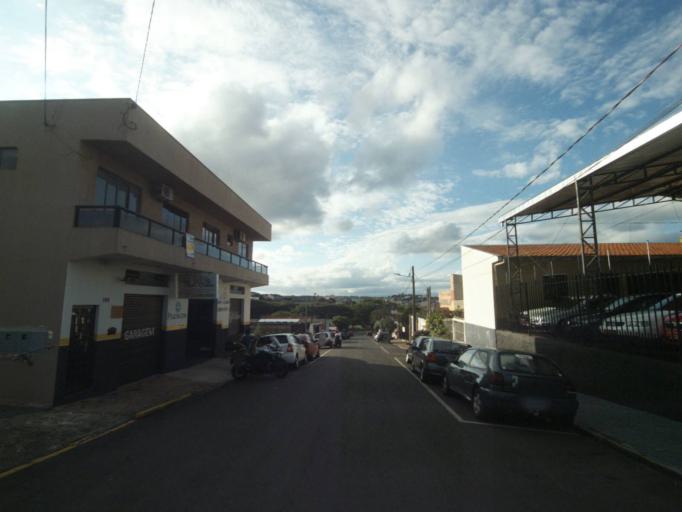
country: BR
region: Parana
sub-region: Telemaco Borba
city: Telemaco Borba
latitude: -24.3329
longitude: -50.6245
